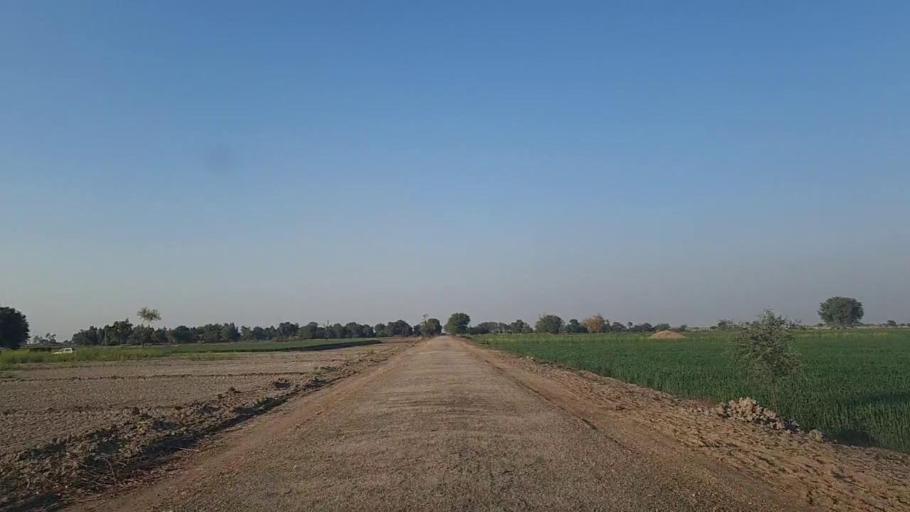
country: PK
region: Sindh
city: Jam Sahib
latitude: 26.3032
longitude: 68.6704
